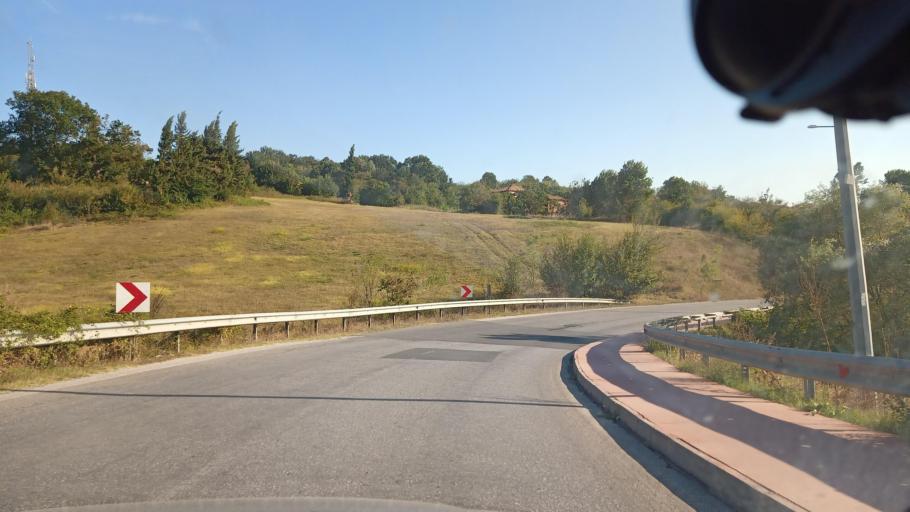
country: TR
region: Kocaeli
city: Kaymaz
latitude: 40.8601
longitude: 30.2788
